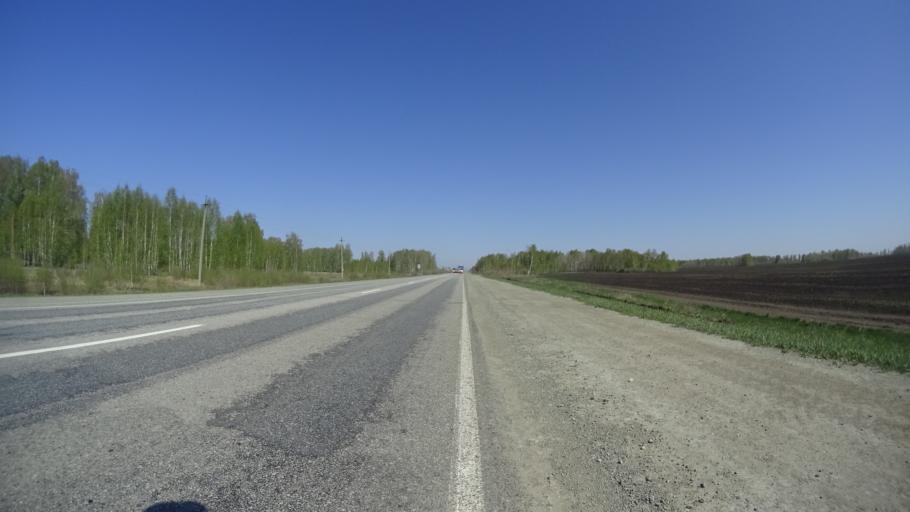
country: RU
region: Chelyabinsk
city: Troitsk
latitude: 54.1808
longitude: 61.4348
